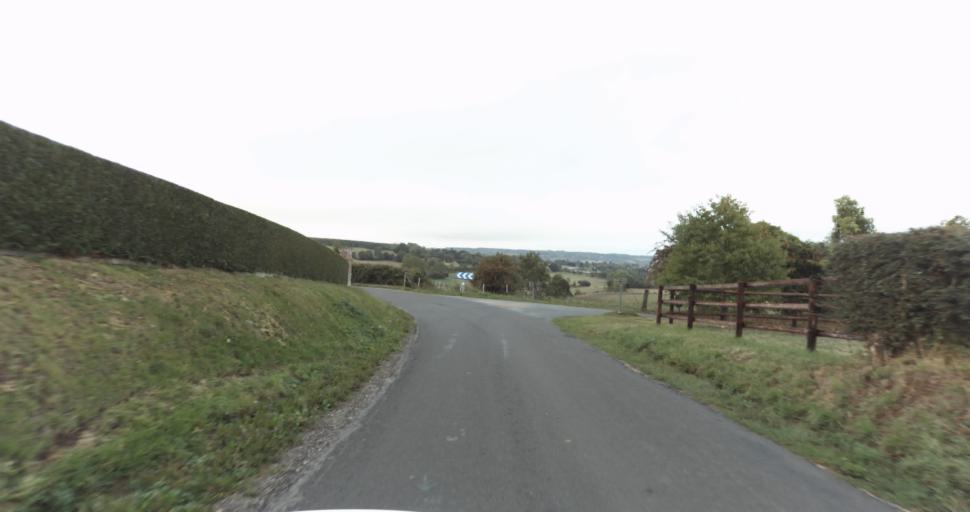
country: FR
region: Lower Normandy
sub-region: Departement de l'Orne
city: Vimoutiers
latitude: 48.9101
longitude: 0.1038
